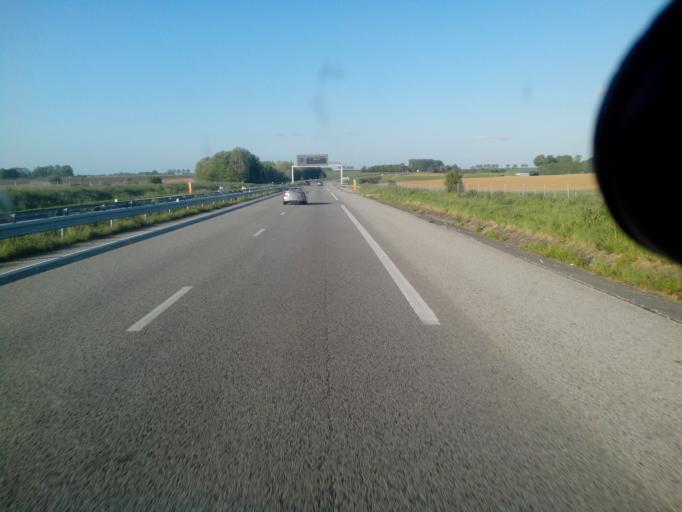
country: FR
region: Haute-Normandie
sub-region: Departement de la Seine-Maritime
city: Fauville-en-Caux
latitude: 49.6242
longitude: 0.6007
